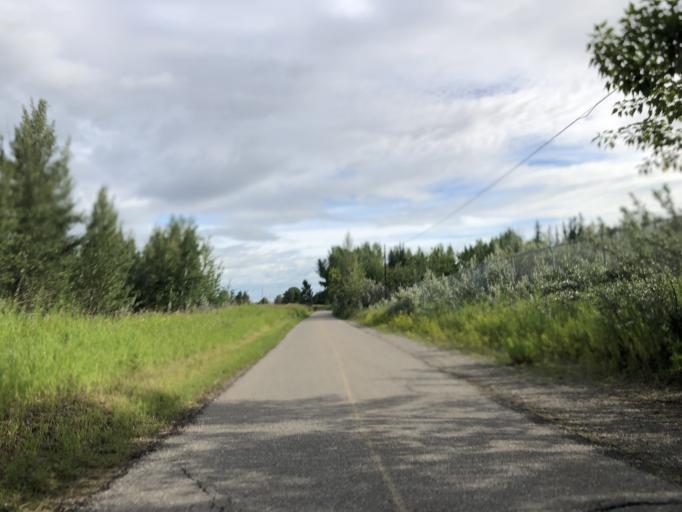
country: CA
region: Alberta
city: Calgary
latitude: 51.0250
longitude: -114.0115
